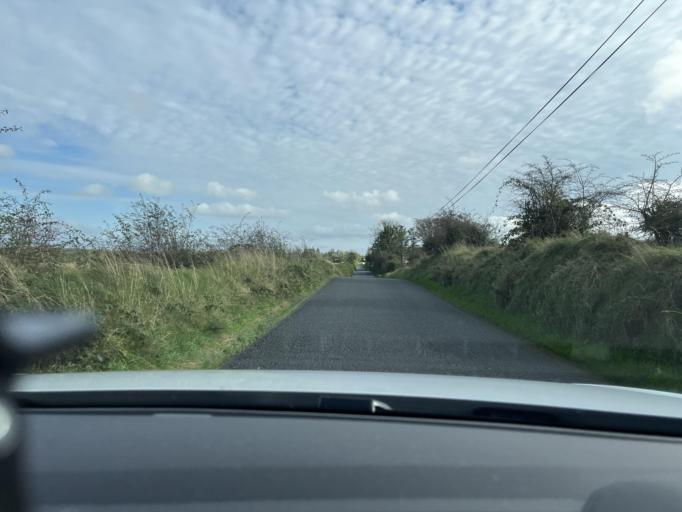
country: IE
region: Connaught
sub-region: Sligo
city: Ballymote
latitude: 54.0814
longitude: -8.4226
